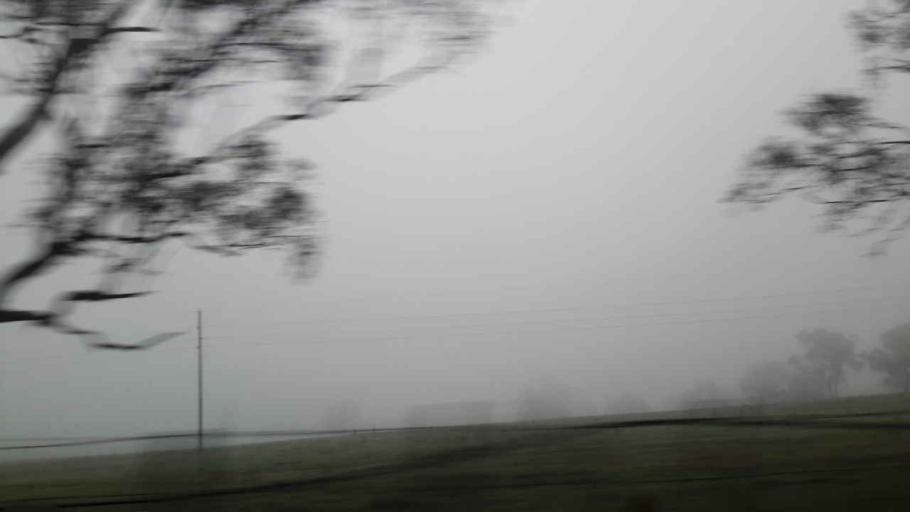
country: AU
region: New South Wales
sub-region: Wollondilly
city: Douglas Park
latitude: -34.2069
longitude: 150.7195
